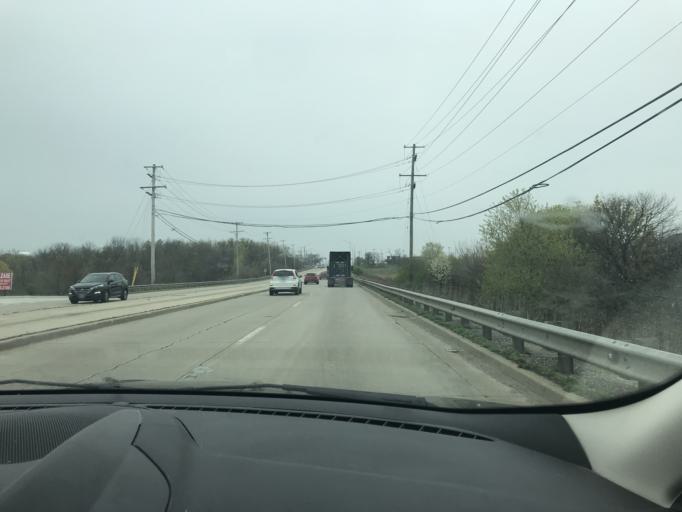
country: US
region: Illinois
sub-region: Kane County
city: Aurora
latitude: 41.7214
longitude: -88.2779
